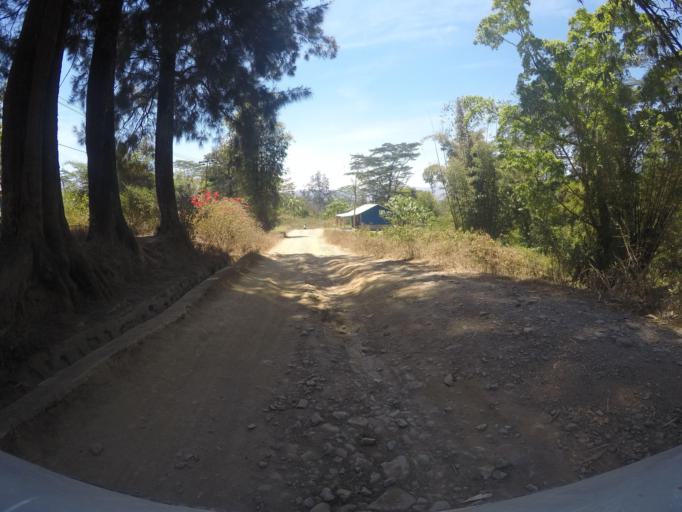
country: TL
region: Ermera
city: Gleno
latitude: -8.7327
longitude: 125.4134
